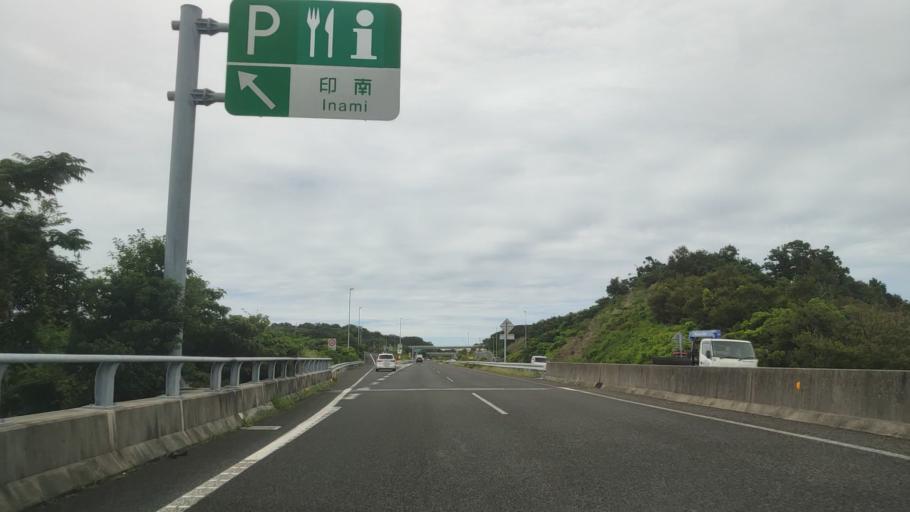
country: JP
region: Wakayama
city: Gobo
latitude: 33.8094
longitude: 135.2411
